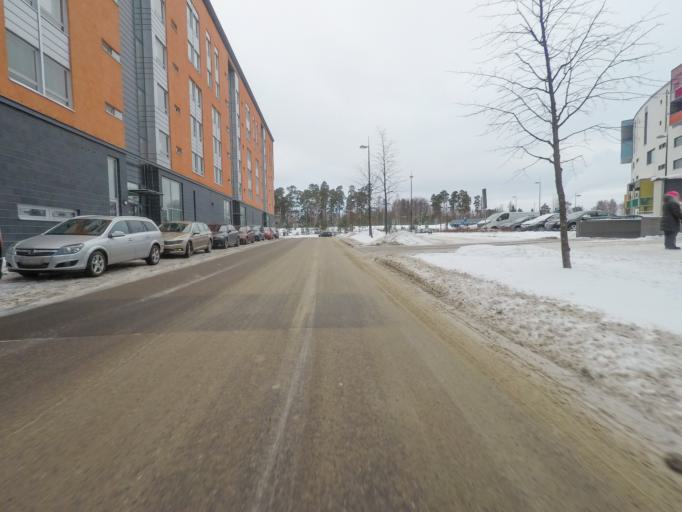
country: FI
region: Uusimaa
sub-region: Helsinki
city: Vantaa
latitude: 60.2073
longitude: 25.1582
